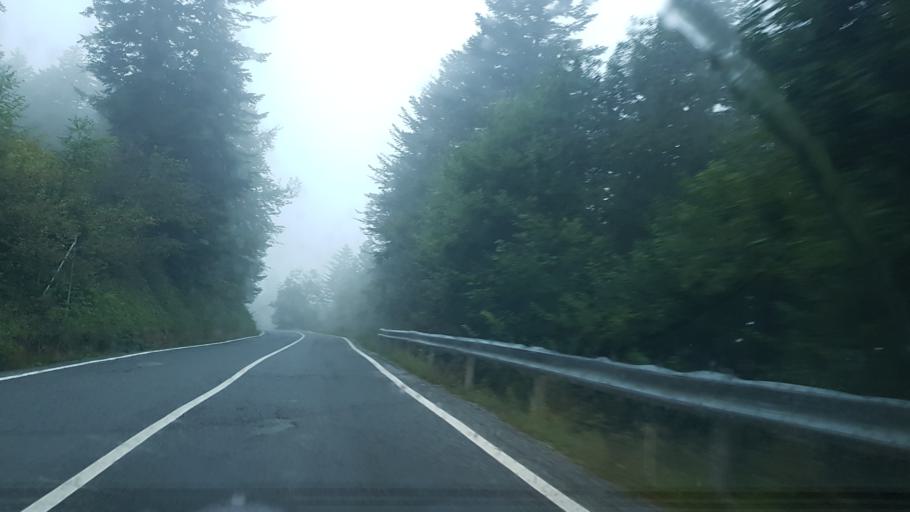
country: IT
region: Piedmont
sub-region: Provincia di Cuneo
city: Frabosa Soprana
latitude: 44.2587
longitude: 7.7759
